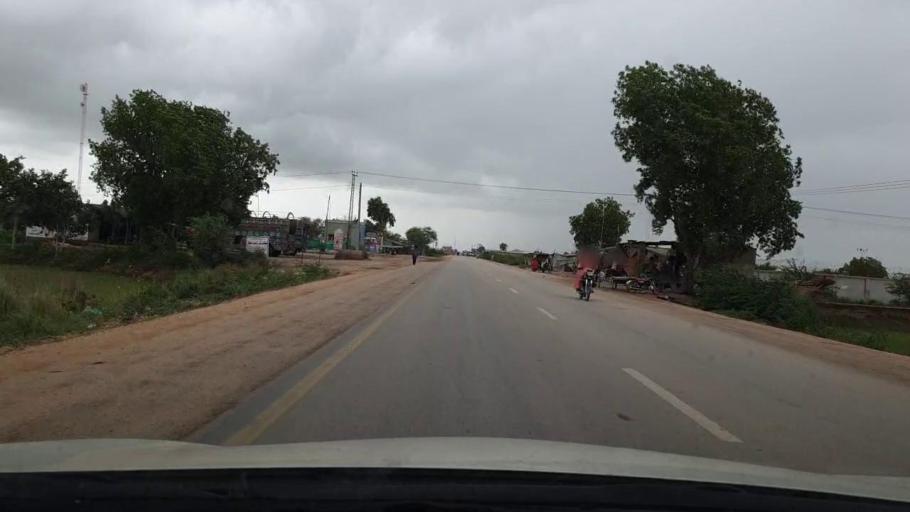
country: PK
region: Sindh
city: Kario
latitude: 24.6526
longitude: 68.5027
